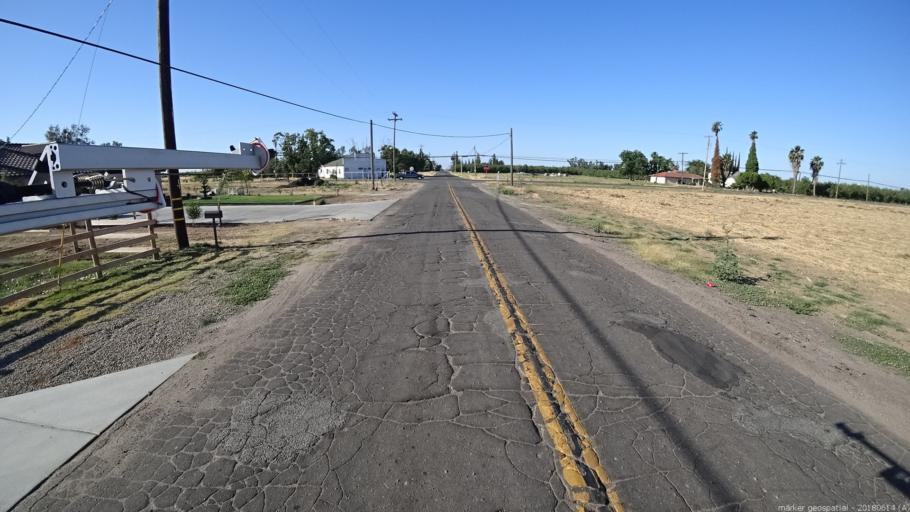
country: US
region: California
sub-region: Madera County
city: Madera
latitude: 36.9535
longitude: -120.1102
